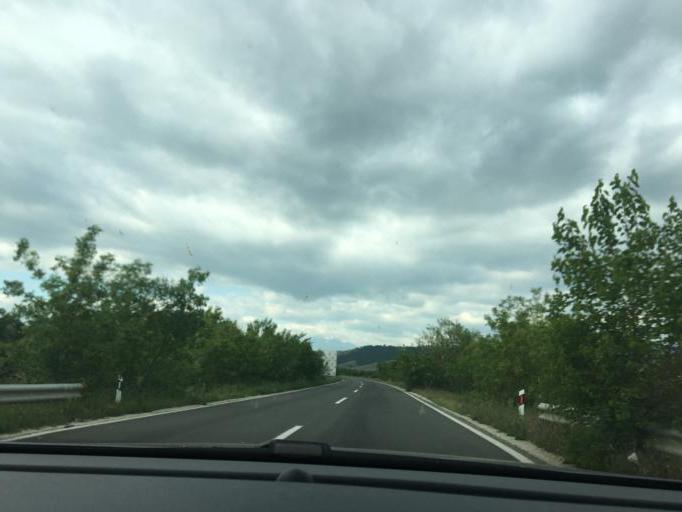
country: MK
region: Prilep
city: Topolcani
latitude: 41.2150
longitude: 21.4257
